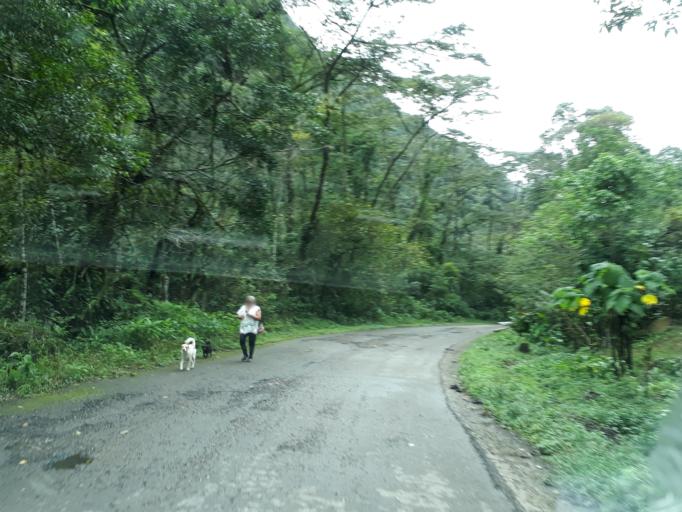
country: CO
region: Boyaca
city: Santa Maria
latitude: 4.7451
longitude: -73.3070
